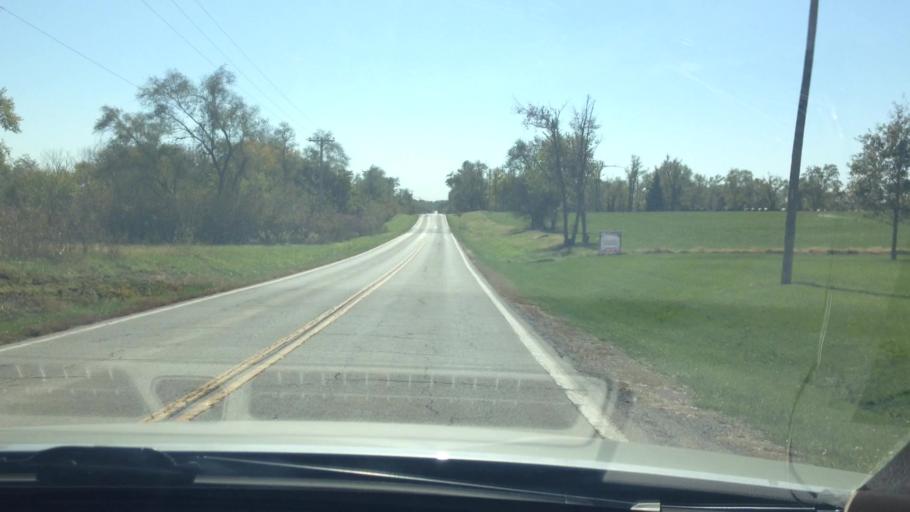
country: US
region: Missouri
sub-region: Clay County
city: Smithville
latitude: 39.3290
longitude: -94.6488
